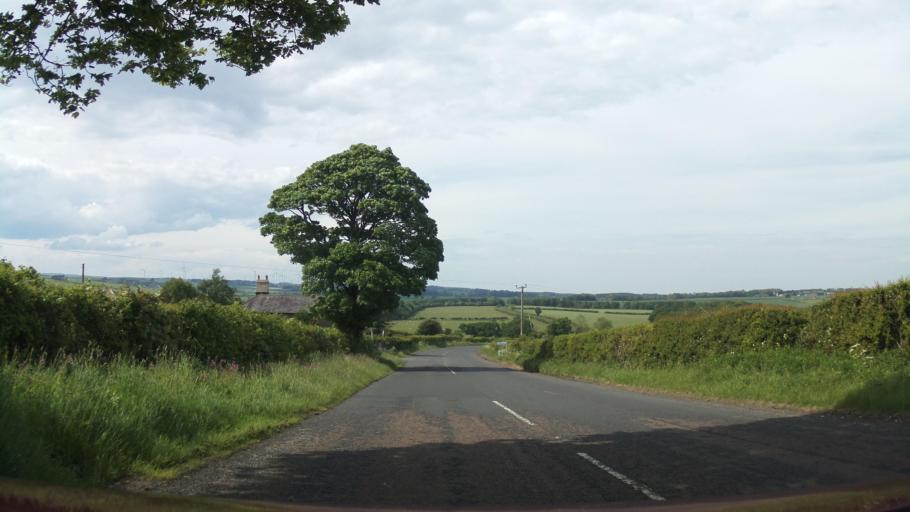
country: GB
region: England
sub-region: Northumberland
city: Alnwick
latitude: 55.4571
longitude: -1.7140
